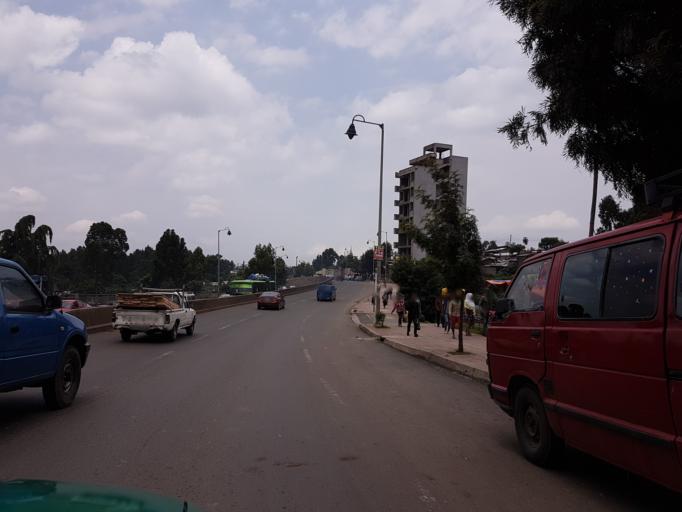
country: ET
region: Adis Abeba
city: Addis Ababa
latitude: 9.0072
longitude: 38.7340
